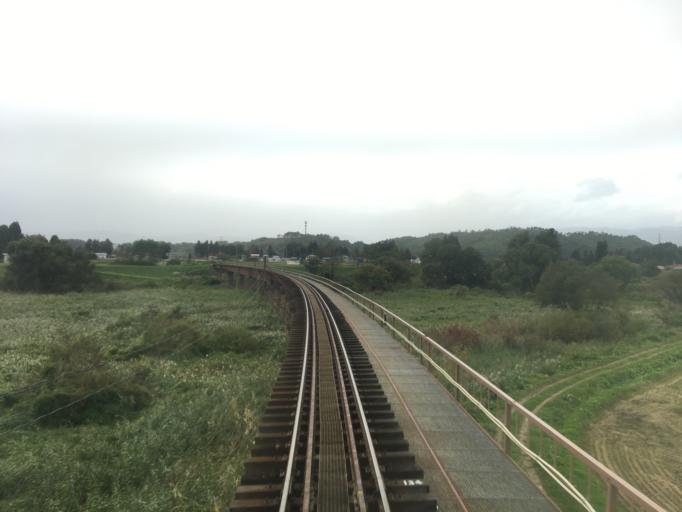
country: JP
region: Yamagata
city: Nagai
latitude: 38.0560
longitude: 140.0717
